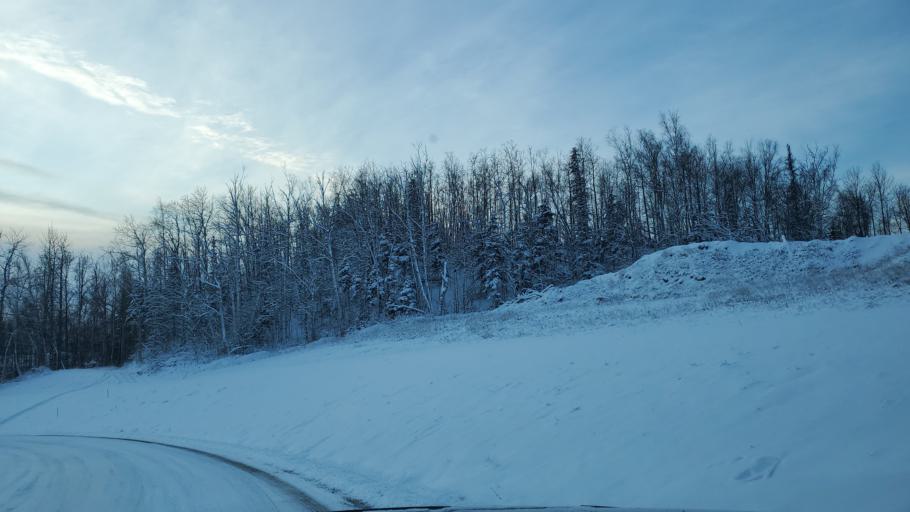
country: US
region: Alaska
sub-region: Matanuska-Susitna Borough
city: Lakes
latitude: 61.5499
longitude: -149.3293
